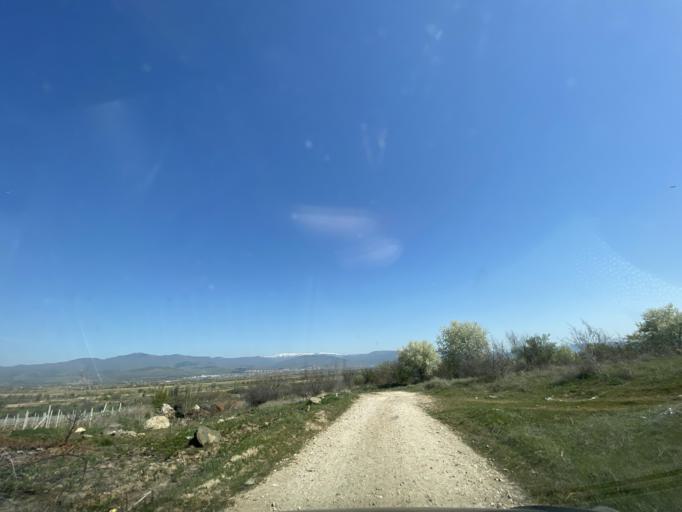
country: MK
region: Zrnovci
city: Zrnovci
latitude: 41.8506
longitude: 22.3893
